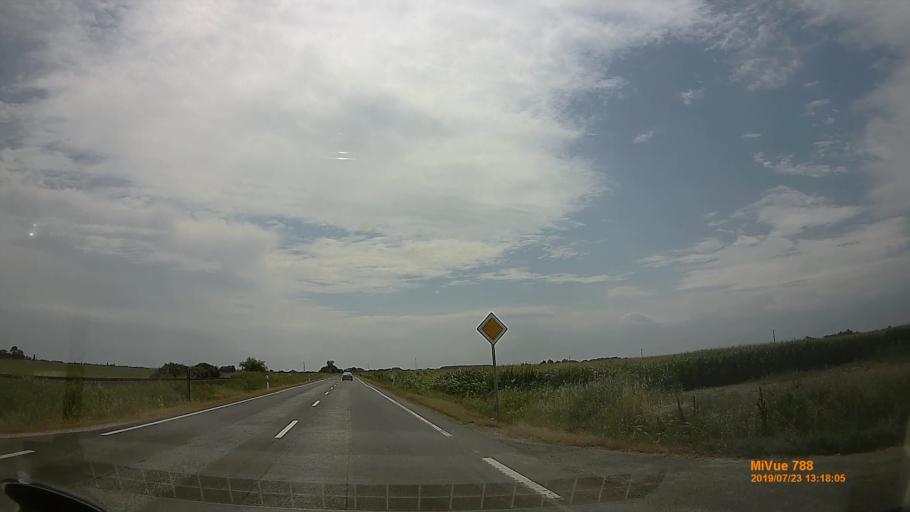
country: HU
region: Hajdu-Bihar
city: Polgar
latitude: 47.8903
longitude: 21.1520
